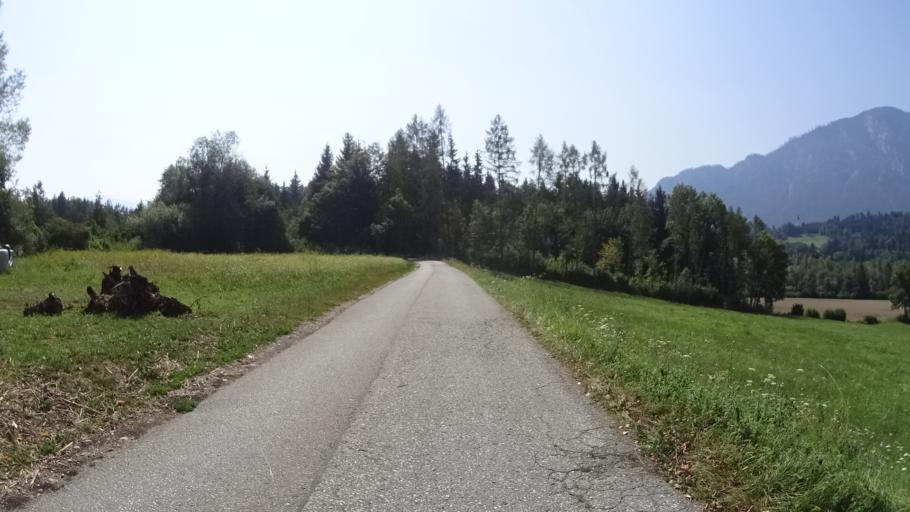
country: AT
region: Carinthia
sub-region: Politischer Bezirk Volkermarkt
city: Gallizien
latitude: 46.5629
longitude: 14.5459
